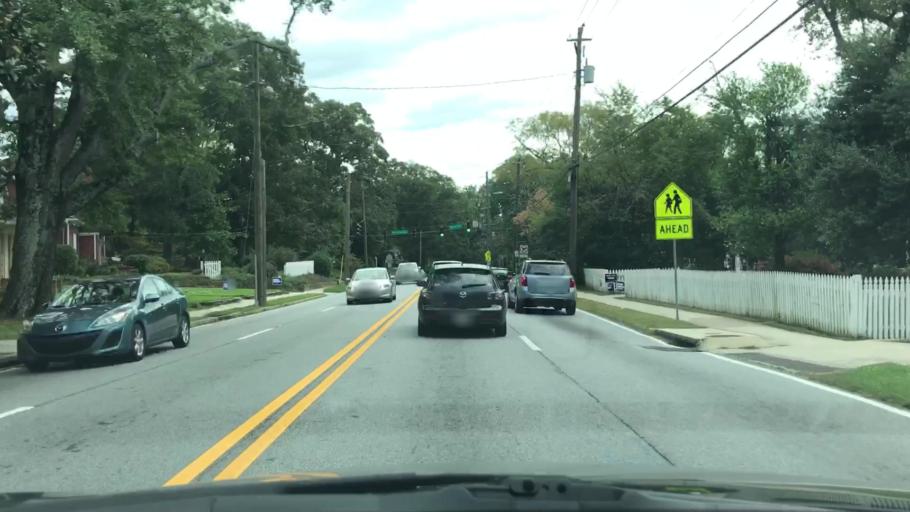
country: US
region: Georgia
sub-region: DeKalb County
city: Decatur
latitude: 33.7825
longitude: -84.3003
